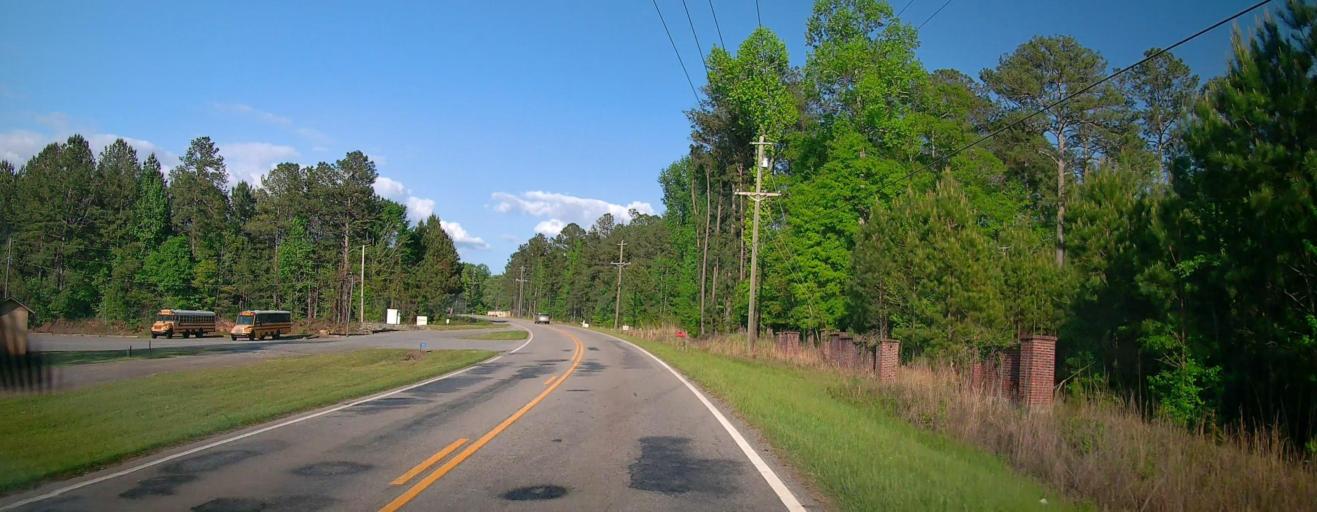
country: US
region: Georgia
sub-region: Putnam County
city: Eatonton
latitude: 33.2383
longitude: -83.3121
